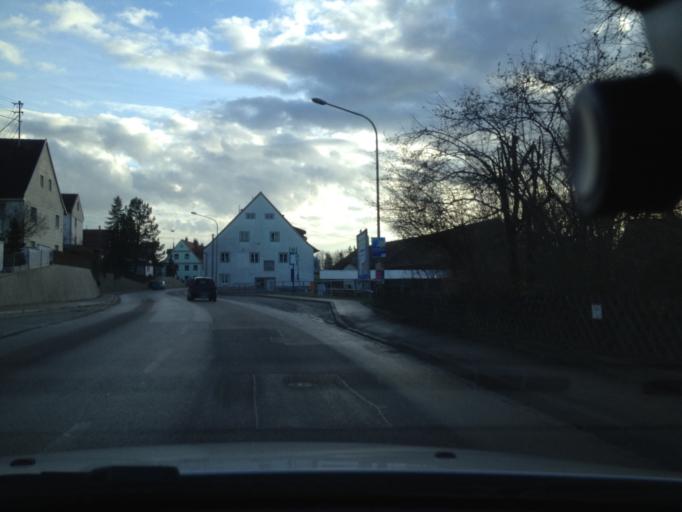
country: DE
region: Bavaria
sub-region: Swabia
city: Schwabmunchen
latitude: 48.1883
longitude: 10.7530
